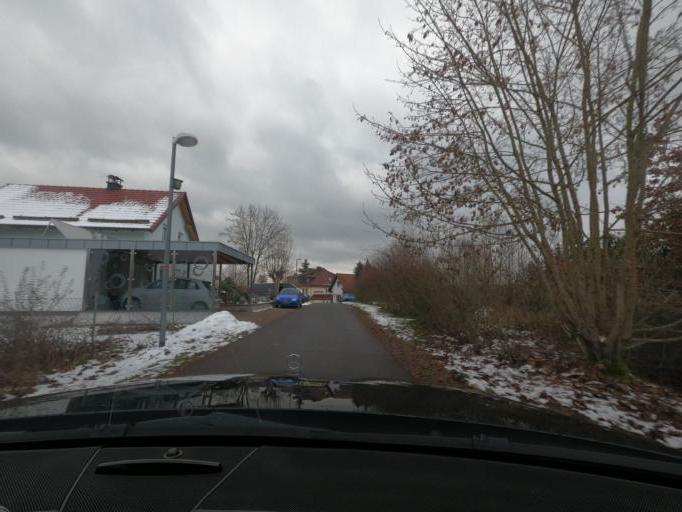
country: DE
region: Thuringia
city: Finsterbergen
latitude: 50.8309
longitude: 10.5898
